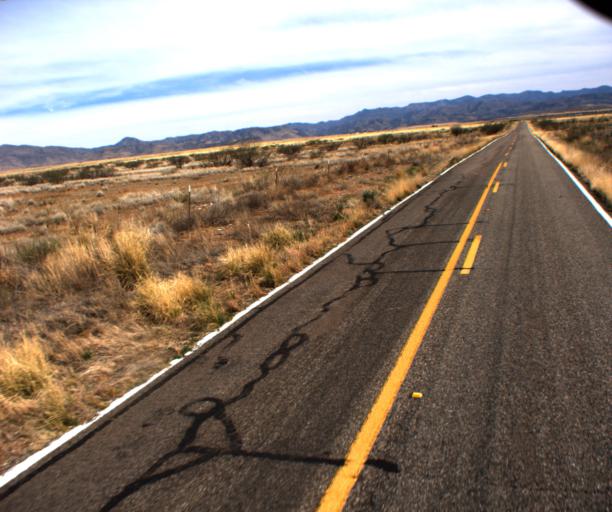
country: US
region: Arizona
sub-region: Cochise County
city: Willcox
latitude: 32.0489
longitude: -109.4898
